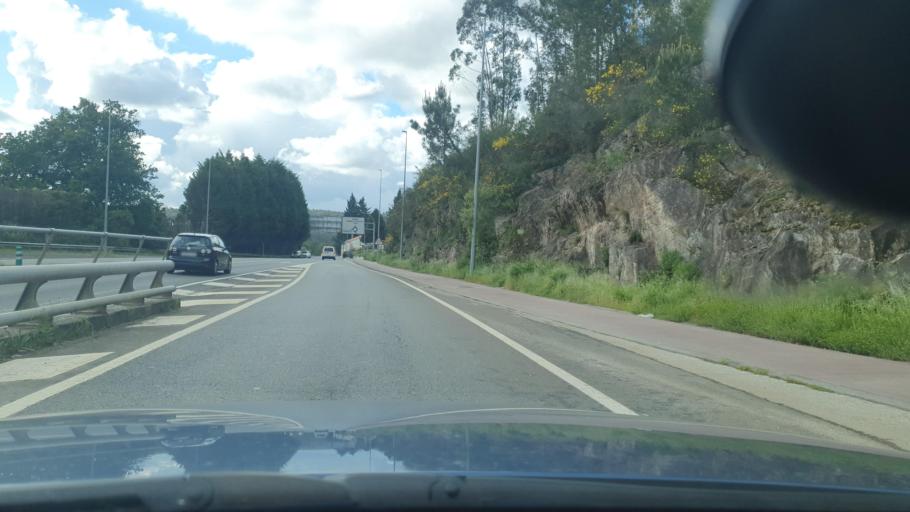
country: ES
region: Galicia
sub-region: Provincia da Coruna
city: Santiago de Compostela
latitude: 42.8706
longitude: -8.5777
